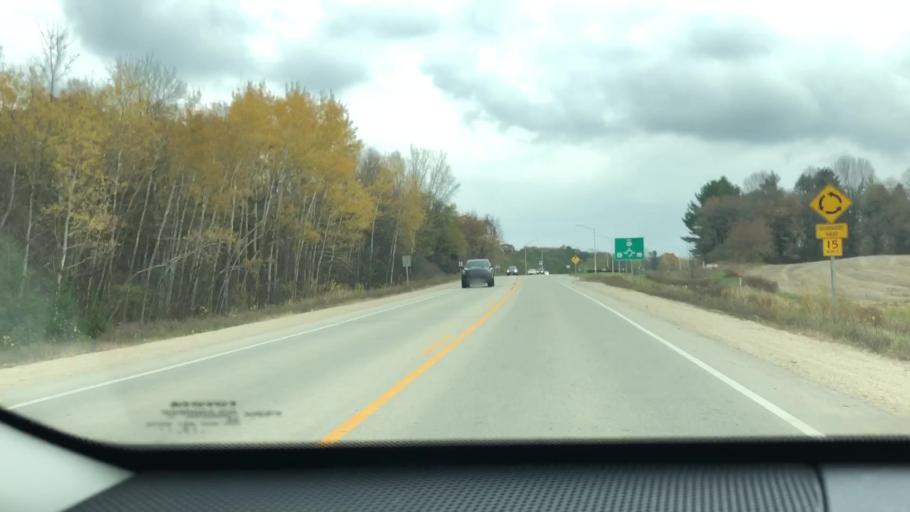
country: US
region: Wisconsin
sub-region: Brown County
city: Oneida
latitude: 44.4992
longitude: -88.1532
